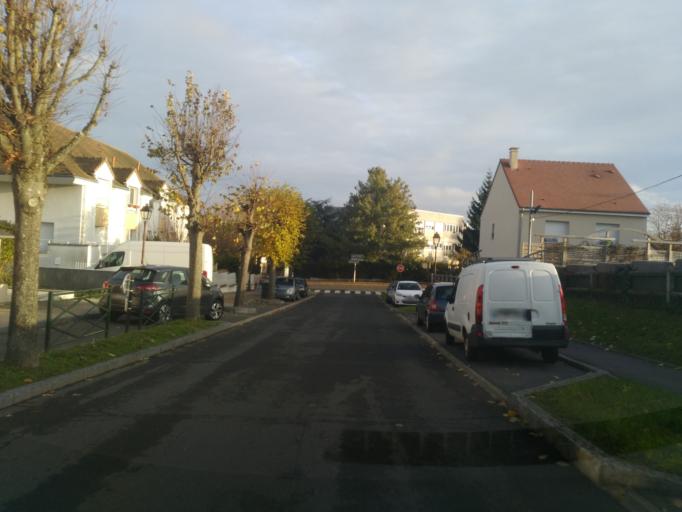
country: FR
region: Ile-de-France
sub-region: Departement des Yvelines
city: Fourqueux
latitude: 48.8905
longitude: 2.0638
